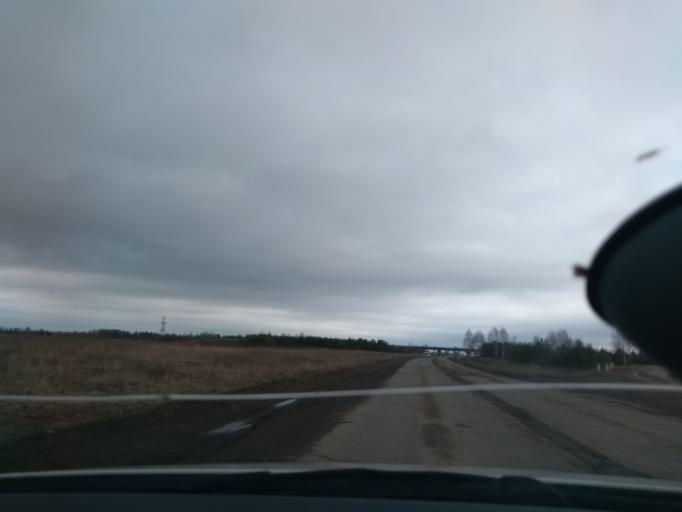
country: RU
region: Perm
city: Kungur
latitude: 57.4010
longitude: 56.8839
